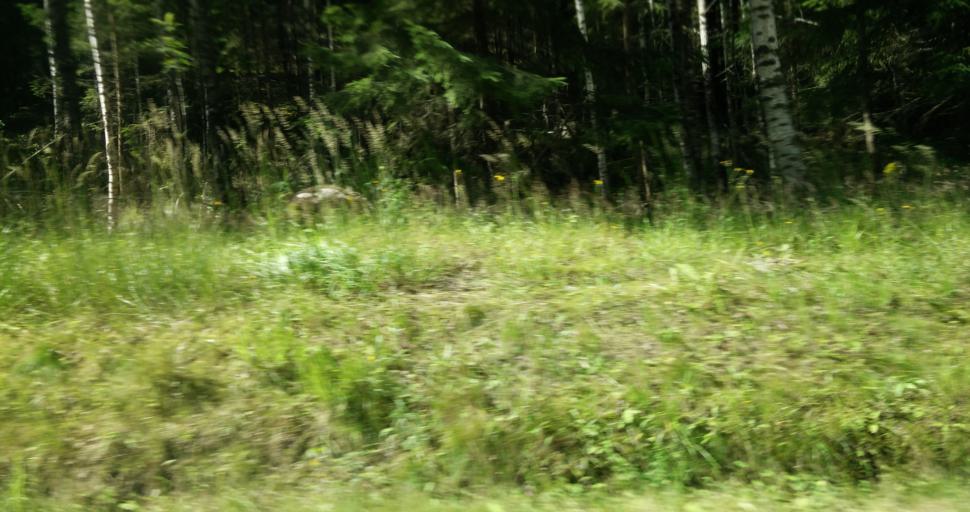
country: SE
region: Vaermland
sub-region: Hagfors Kommun
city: Ekshaerad
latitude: 60.0977
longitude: 13.4493
